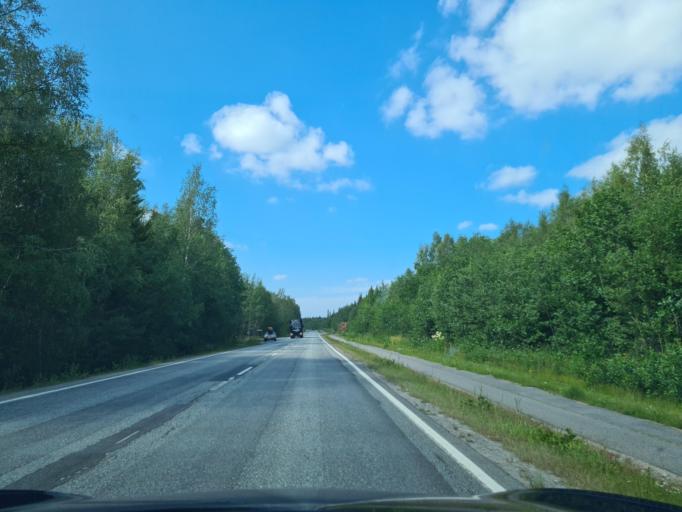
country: FI
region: Ostrobothnia
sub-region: Vaasa
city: Replot
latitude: 63.2002
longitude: 21.5342
